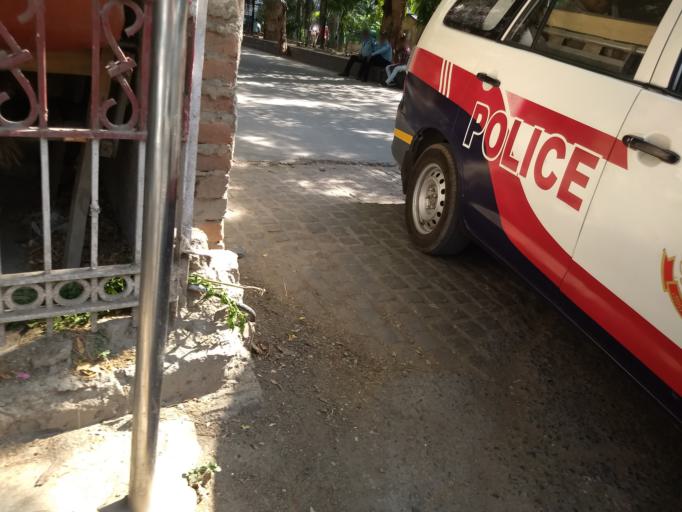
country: IN
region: NCT
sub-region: New Delhi
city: New Delhi
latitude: 28.5671
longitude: 77.2032
